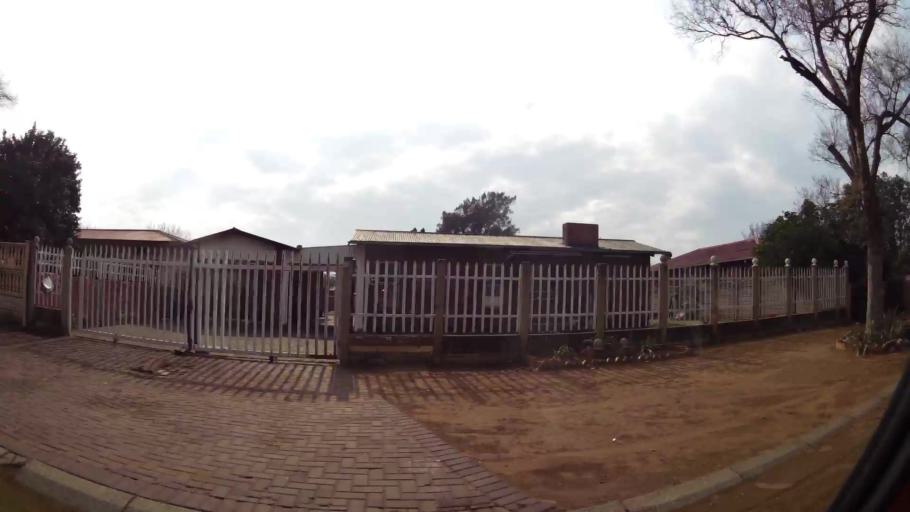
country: ZA
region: Gauteng
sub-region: Sedibeng District Municipality
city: Vanderbijlpark
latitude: -26.6899
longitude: 27.8405
